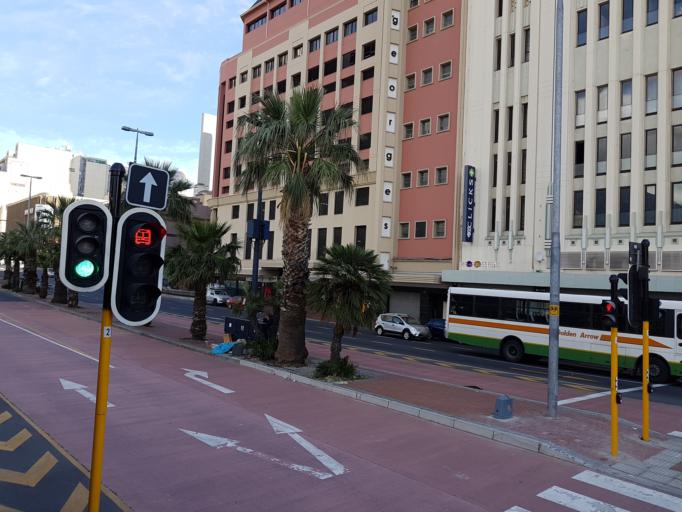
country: ZA
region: Western Cape
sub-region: City of Cape Town
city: Cape Town
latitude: -33.9211
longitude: 18.4245
